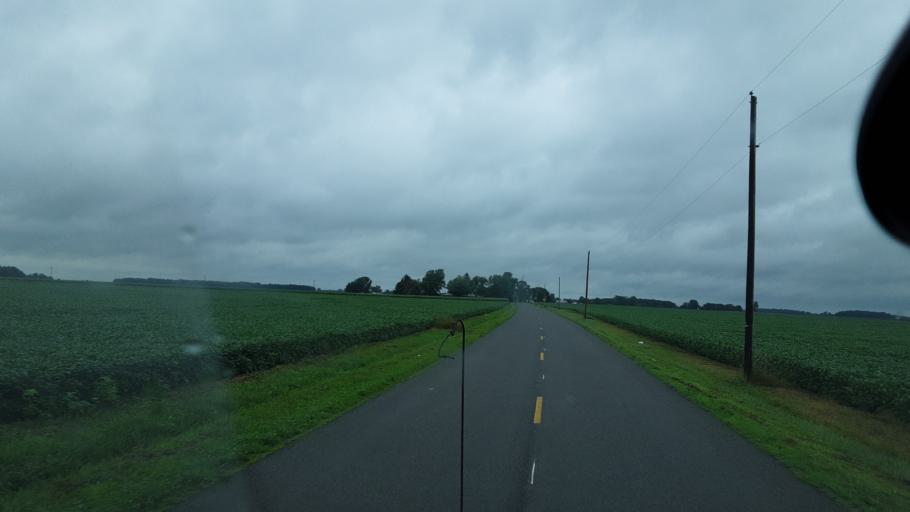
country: US
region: Ohio
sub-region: Van Wert County
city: Convoy
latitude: 40.8185
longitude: -84.6774
